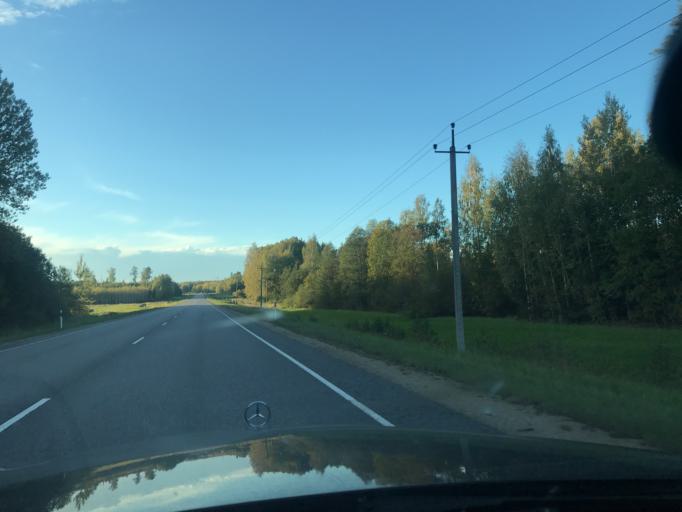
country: EE
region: Vorumaa
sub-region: Voru linn
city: Voru
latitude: 57.8420
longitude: 27.0510
